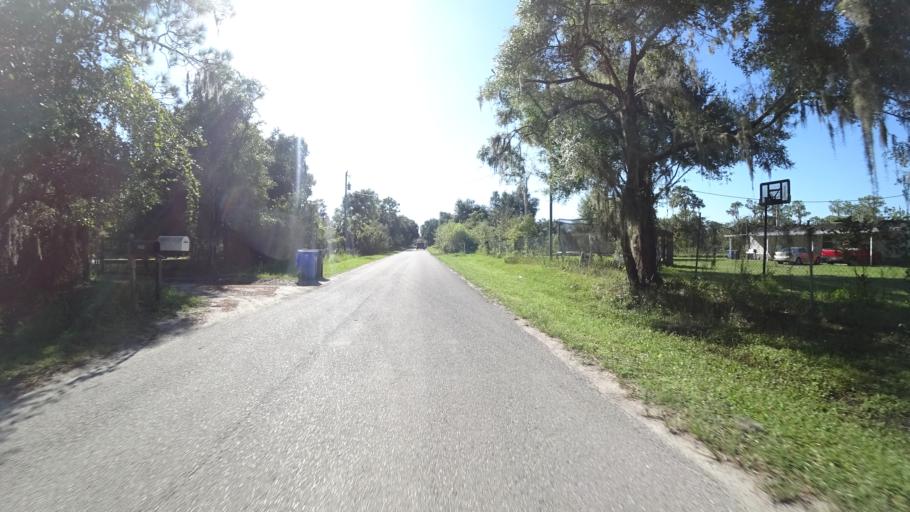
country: US
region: Florida
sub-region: Hillsborough County
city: Sun City Center
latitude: 27.6492
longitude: -82.3601
